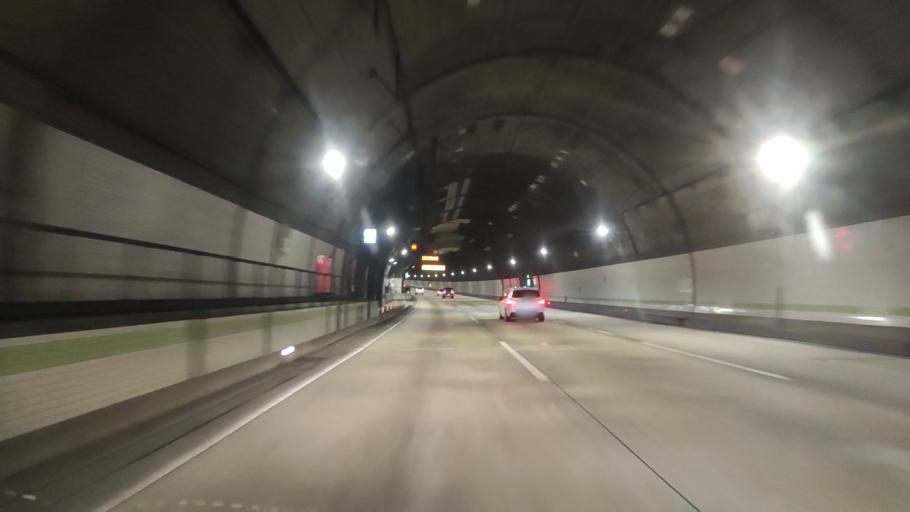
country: JP
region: Hyogo
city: Akashi
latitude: 34.6396
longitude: 135.0430
